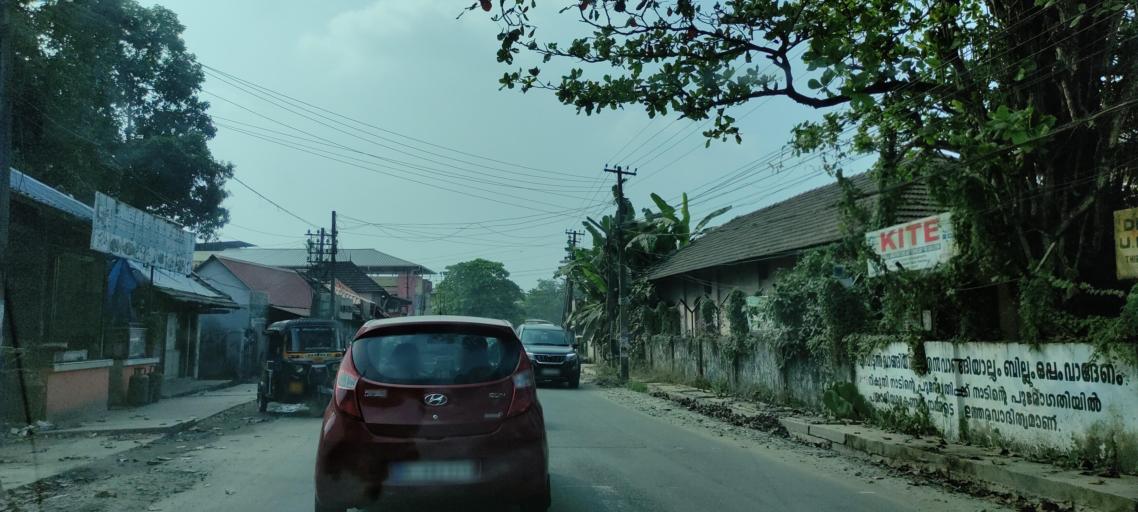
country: IN
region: Kerala
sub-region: Pattanamtitta
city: Tiruvalla
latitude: 9.3781
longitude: 76.5661
